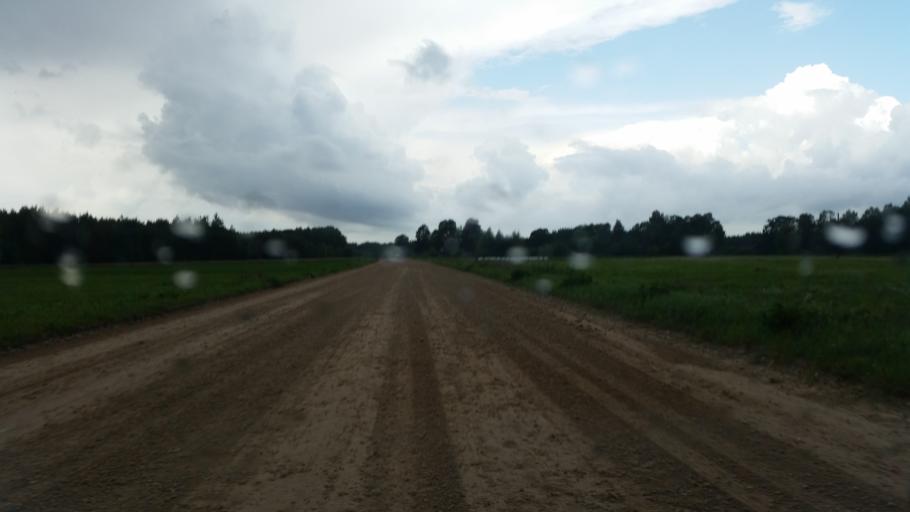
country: LV
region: Vecumnieki
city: Vecumnieki
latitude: 56.4299
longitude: 24.4558
